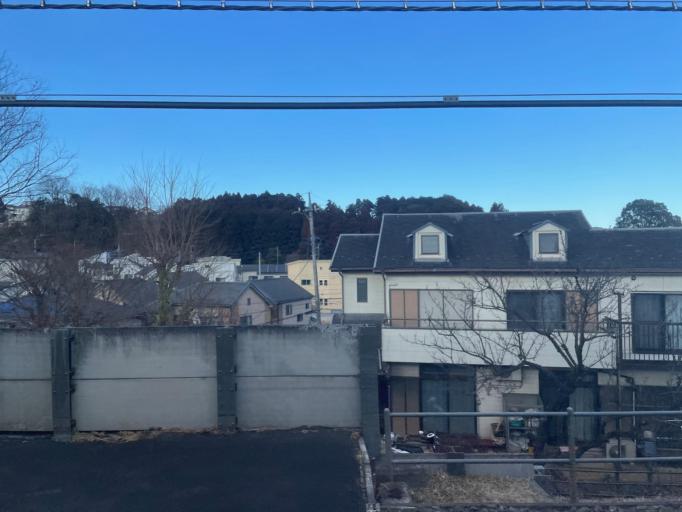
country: JP
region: Tokyo
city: Hachioji
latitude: 35.6447
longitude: 139.3163
